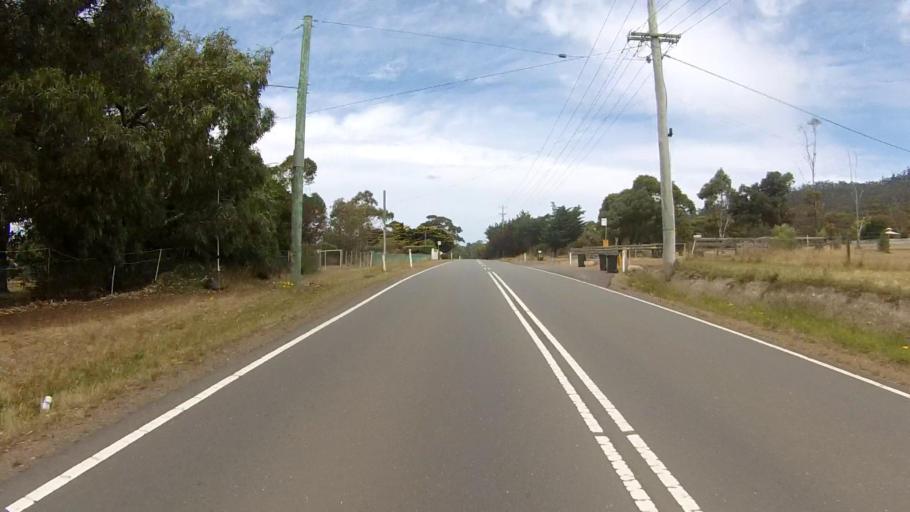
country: AU
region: Tasmania
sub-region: Clarence
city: Acton Park
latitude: -42.8914
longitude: 147.4822
